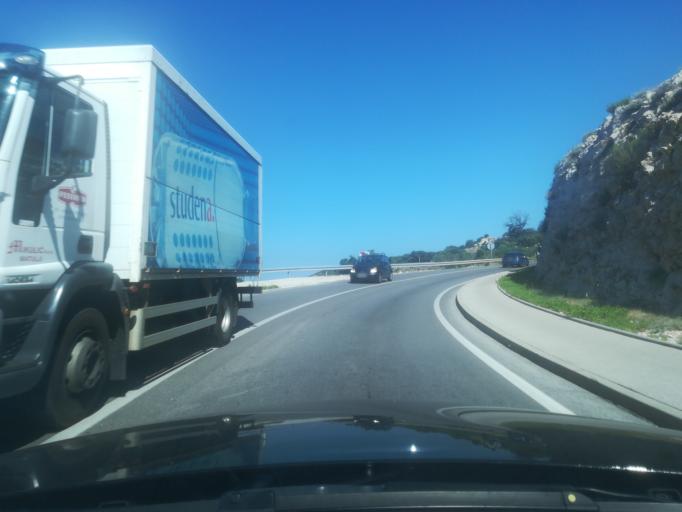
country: HR
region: Primorsko-Goranska
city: Supetarska Draga
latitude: 44.8138
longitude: 14.7165
